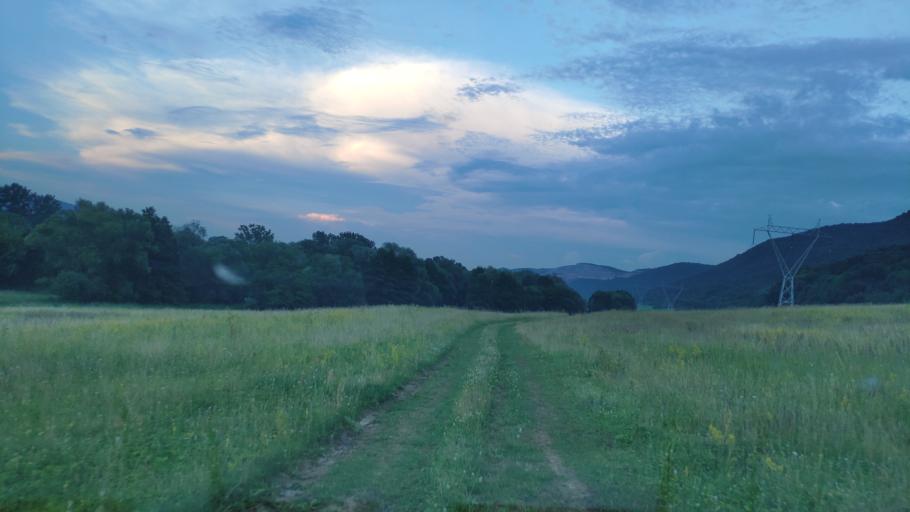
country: SK
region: Kosicky
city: Medzev
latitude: 48.5856
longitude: 20.7510
